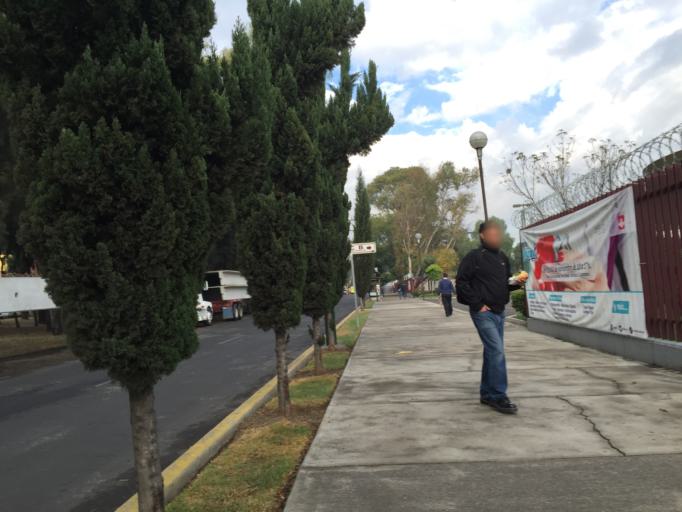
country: MX
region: Mexico
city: Colonia Lindavista
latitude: 19.4986
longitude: -99.1453
